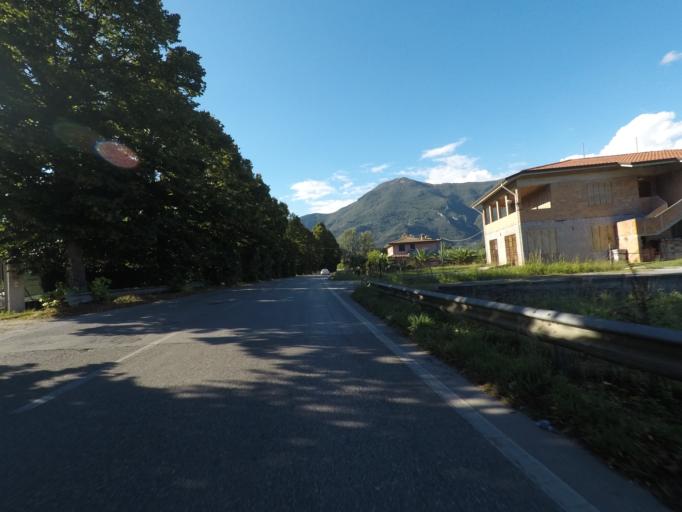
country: IT
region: Tuscany
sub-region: Provincia di Lucca
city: Corsanico-Bargecchia
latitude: 43.9301
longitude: 10.3121
